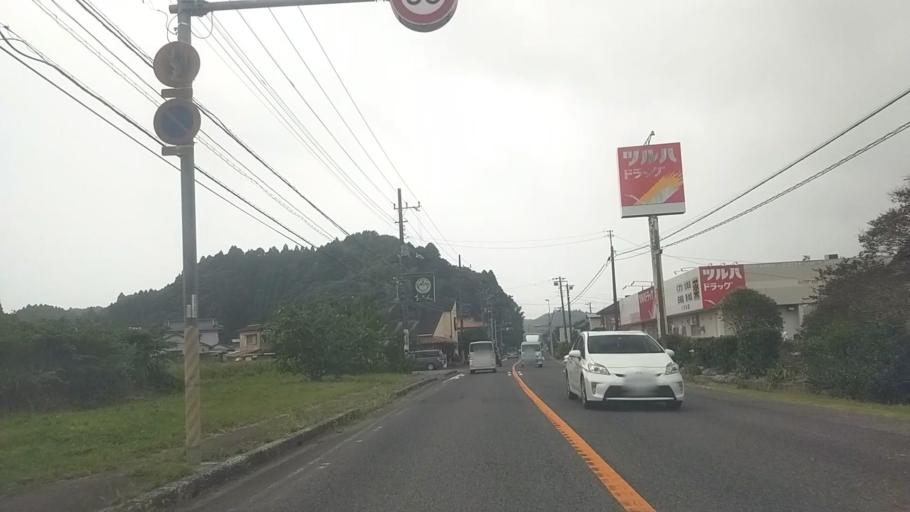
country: JP
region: Chiba
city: Ohara
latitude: 35.2301
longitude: 140.3877
